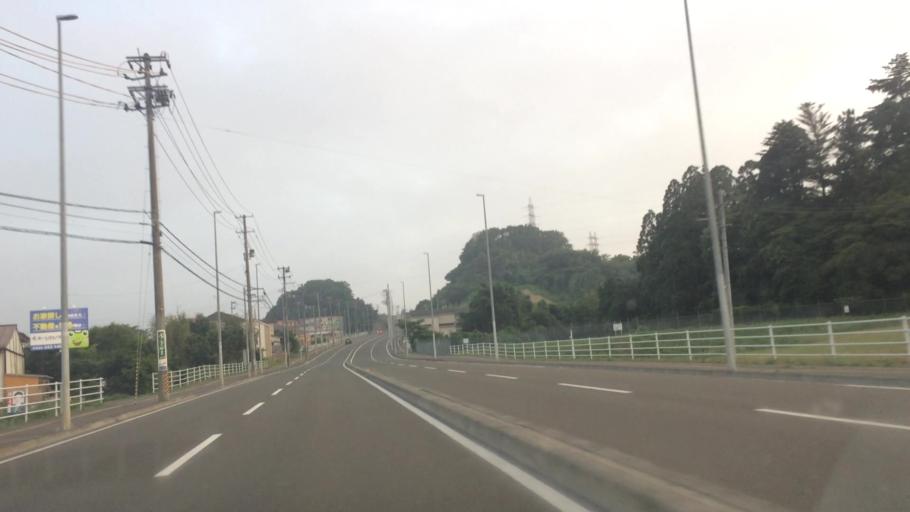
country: JP
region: Miyagi
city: Sendai-shi
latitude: 38.3007
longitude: 140.9201
